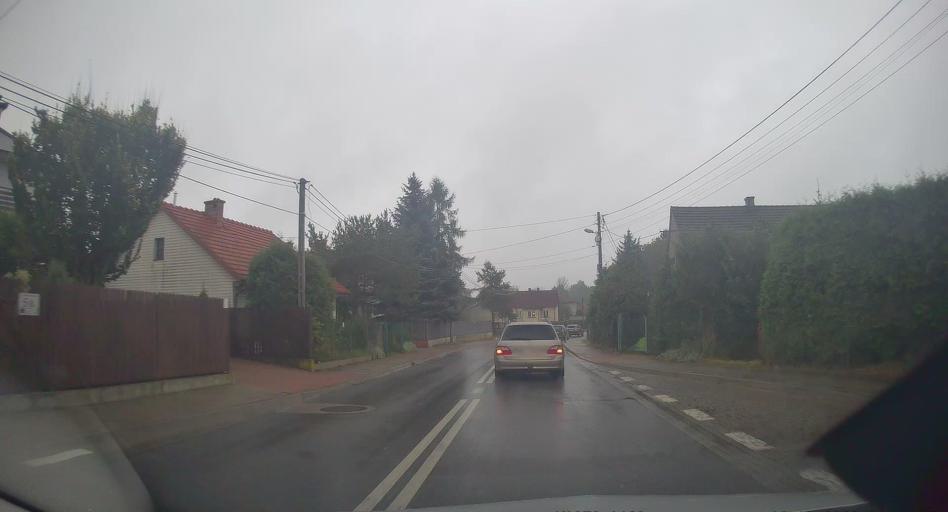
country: PL
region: Lesser Poland Voivodeship
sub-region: Powiat krakowski
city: Ochojno
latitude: 49.9821
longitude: 19.9893
